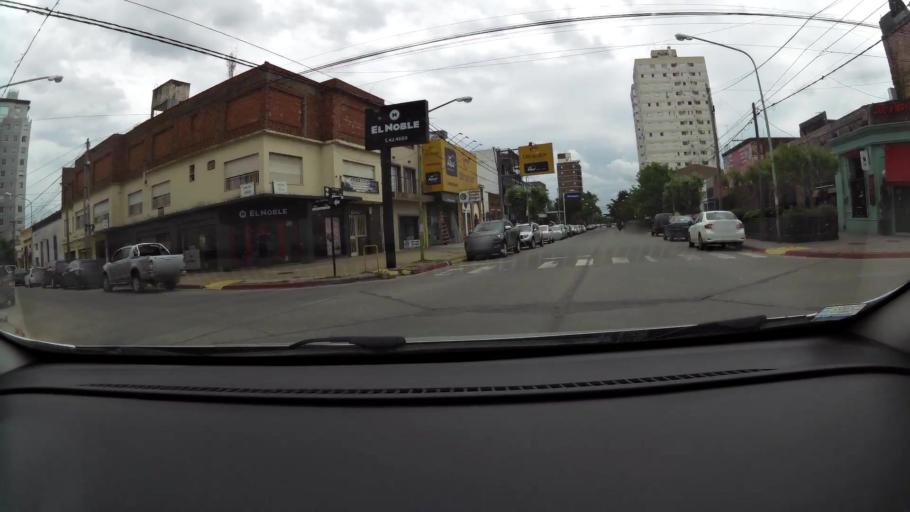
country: AR
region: Buenos Aires
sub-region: Partido de Campana
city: Campana
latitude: -34.1630
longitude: -58.9637
